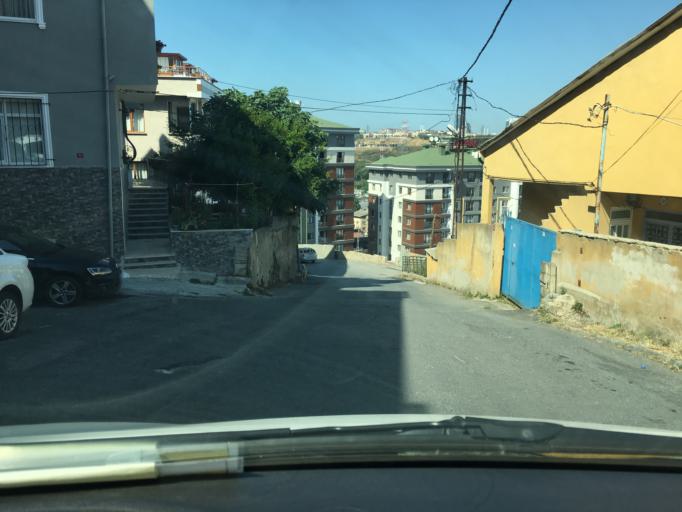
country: TR
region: Istanbul
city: Sisli
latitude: 41.0800
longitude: 28.9463
